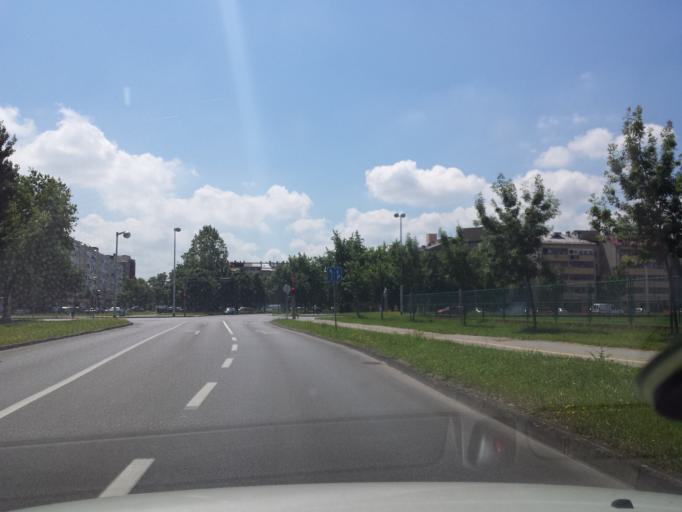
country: HR
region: Grad Zagreb
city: Jankomir
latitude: 45.8028
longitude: 15.8941
